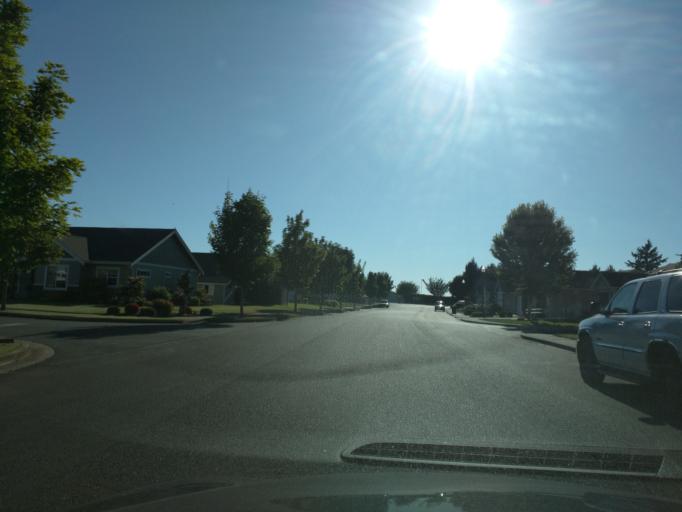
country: US
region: Washington
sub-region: Whatcom County
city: Lynden
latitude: 48.9555
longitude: -122.4502
